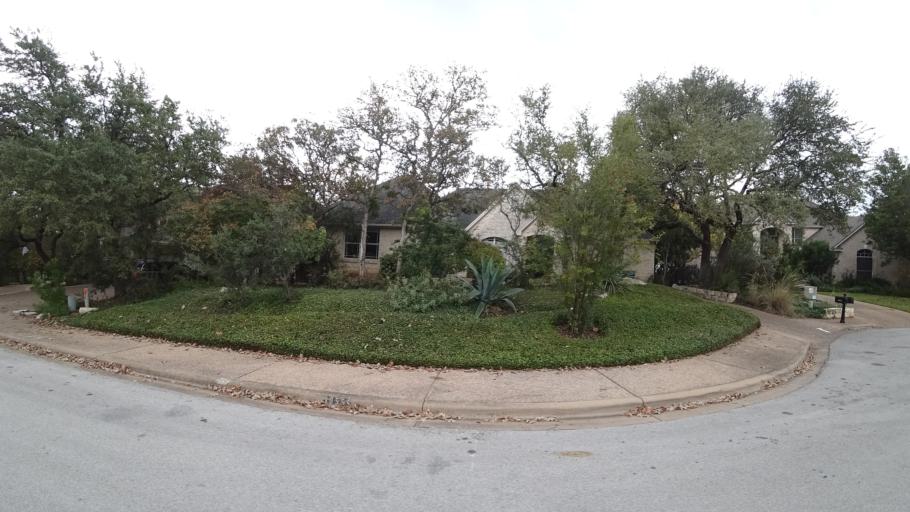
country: US
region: Texas
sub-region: Travis County
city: Barton Creek
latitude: 30.3095
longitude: -97.9002
